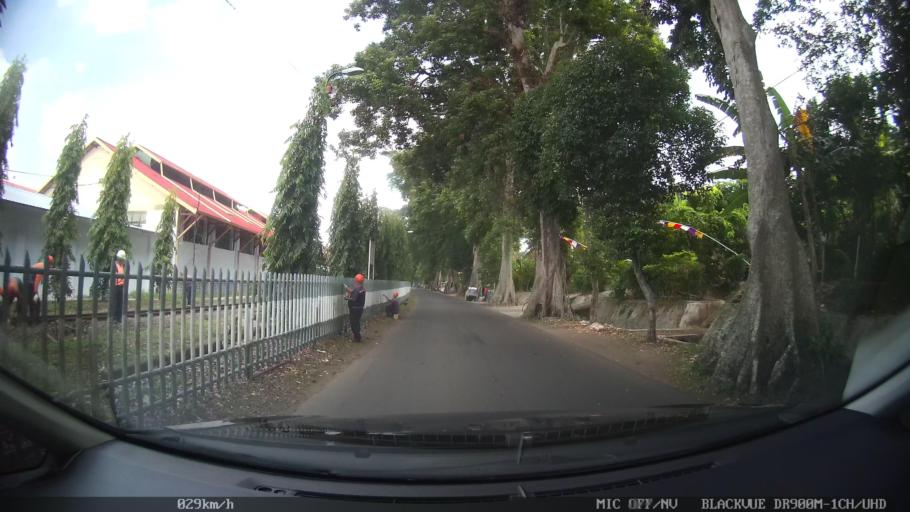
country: ID
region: Daerah Istimewa Yogyakarta
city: Yogyakarta
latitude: -7.7869
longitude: 110.3856
